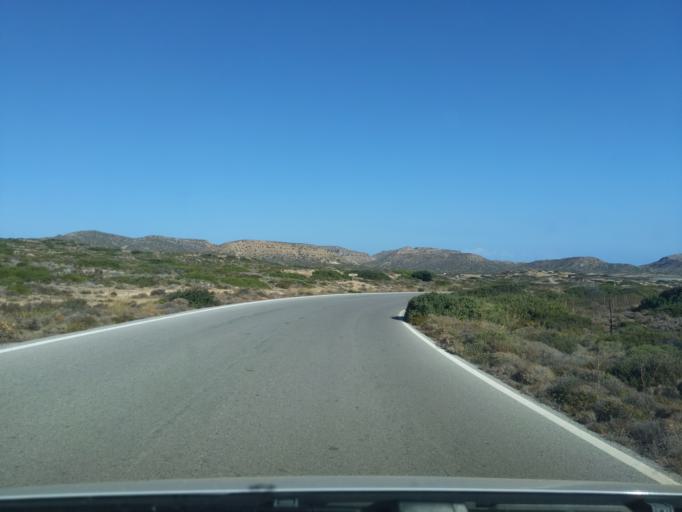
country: GR
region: Crete
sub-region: Nomos Lasithiou
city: Palekastro
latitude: 35.2431
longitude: 26.2487
